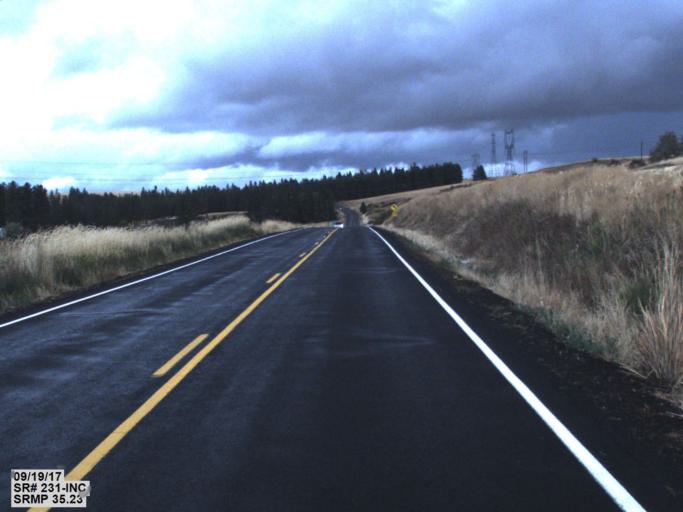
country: US
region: Washington
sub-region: Spokane County
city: Medical Lake
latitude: 47.7280
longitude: -117.8702
